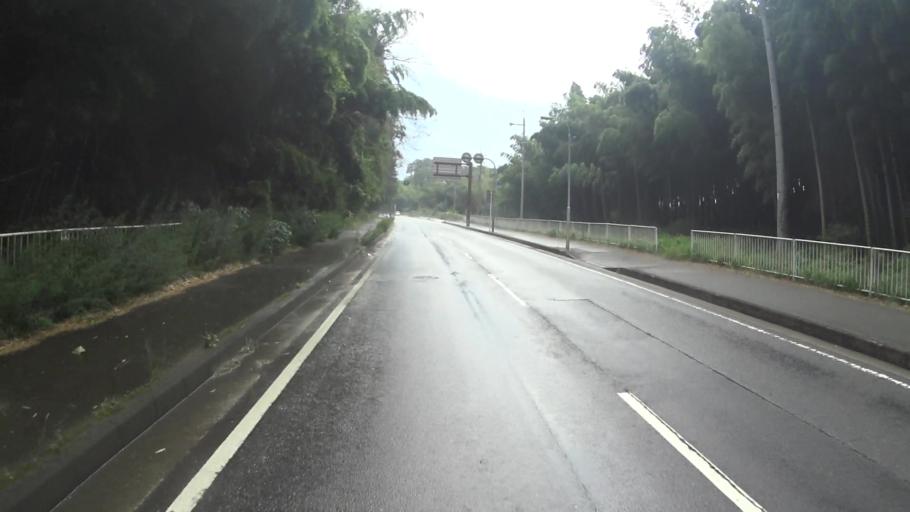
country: JP
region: Kyoto
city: Tanabe
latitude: 34.8134
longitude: 135.7629
